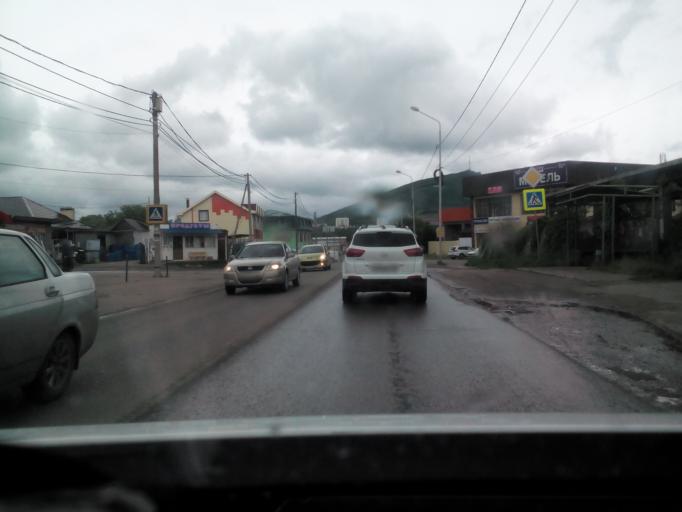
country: RU
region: Stavropol'skiy
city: Pyatigorsk
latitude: 44.0593
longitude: 43.0364
